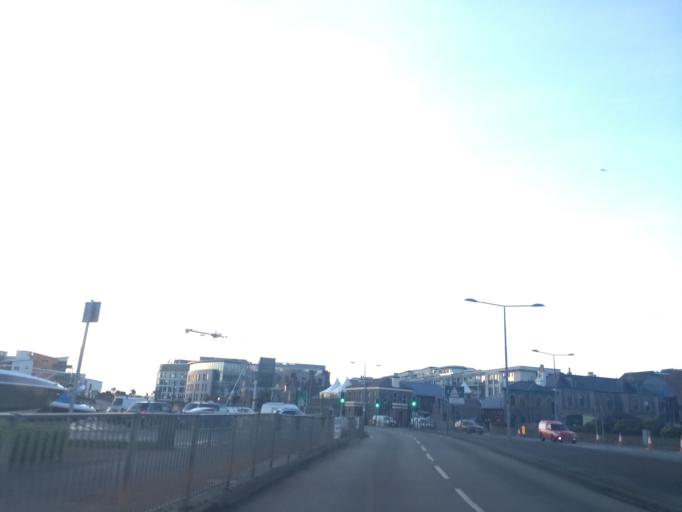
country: JE
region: St Helier
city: Saint Helier
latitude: 49.1819
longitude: -2.1087
